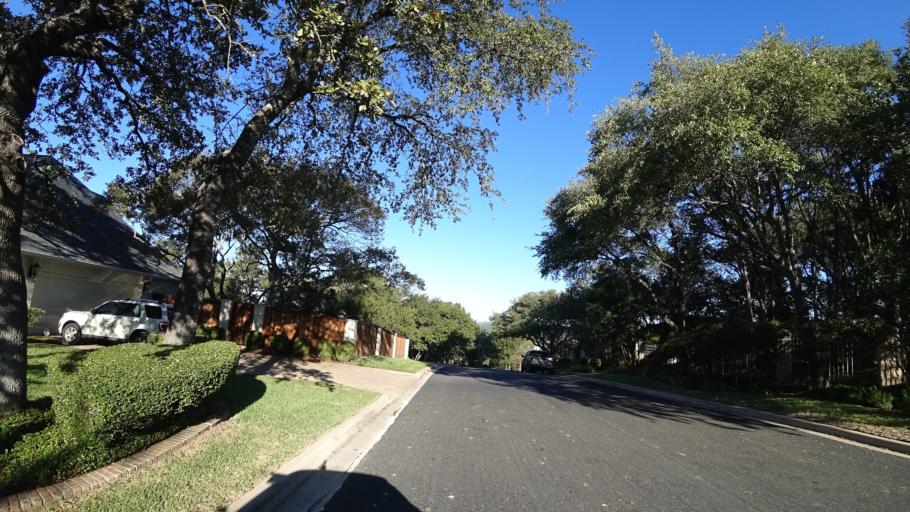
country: US
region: Texas
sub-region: Travis County
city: West Lake Hills
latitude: 30.3285
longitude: -97.8072
